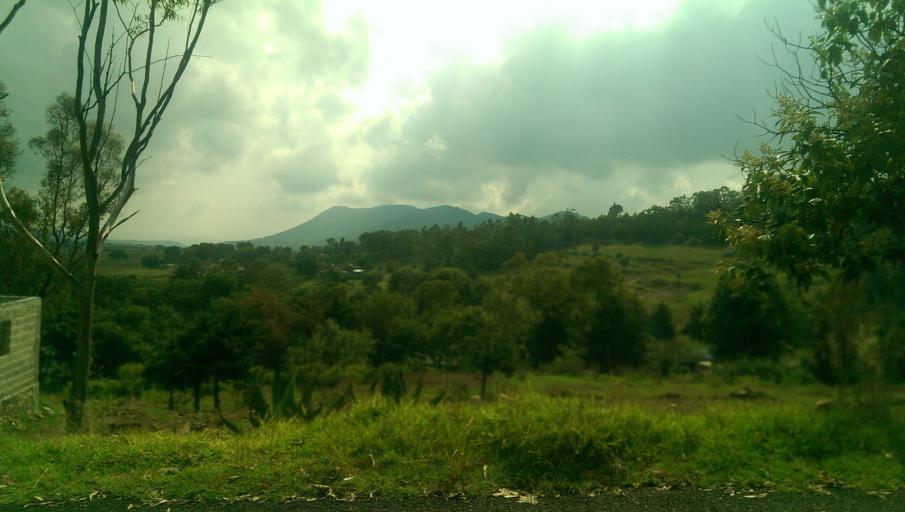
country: MX
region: Mexico
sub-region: Jilotepec
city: Jilotepec de Molina Enriquez
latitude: 19.9459
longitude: -99.4900
